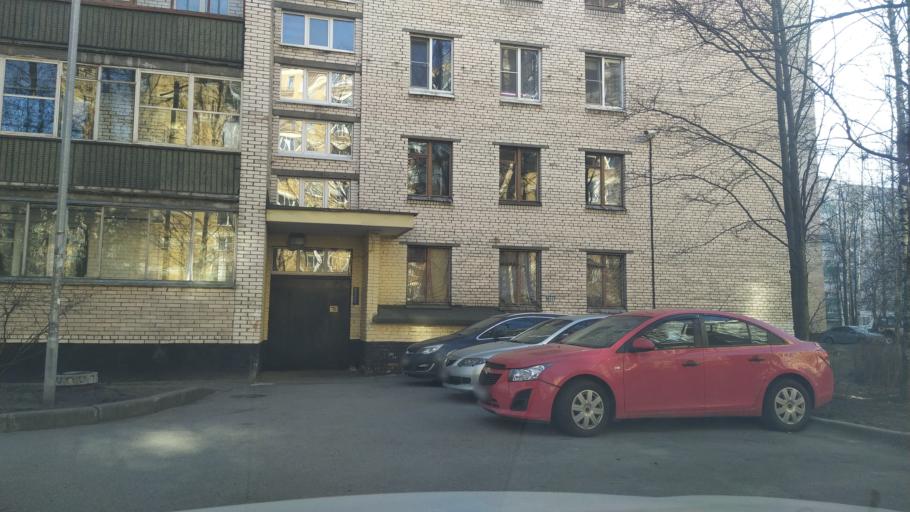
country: RU
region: Leningrad
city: Akademicheskoe
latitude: 60.0170
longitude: 30.3984
